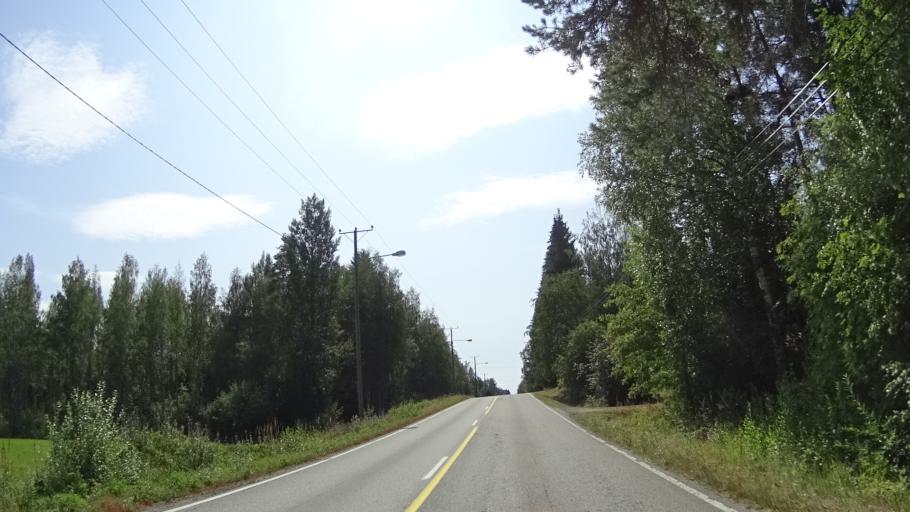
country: FI
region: Pirkanmaa
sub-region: Ylae-Pirkanmaa
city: Maenttae
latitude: 61.8961
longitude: 24.7934
